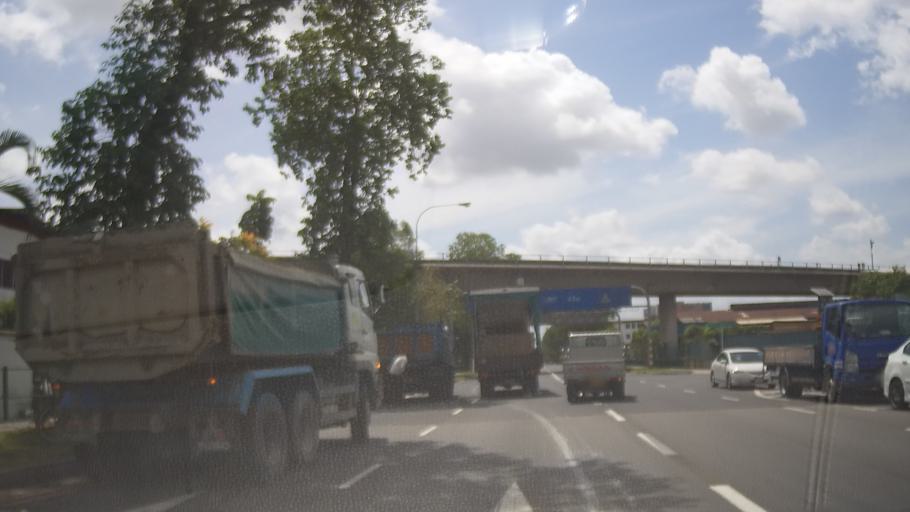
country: MY
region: Johor
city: Johor Bahru
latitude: 1.4220
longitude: 103.7503
